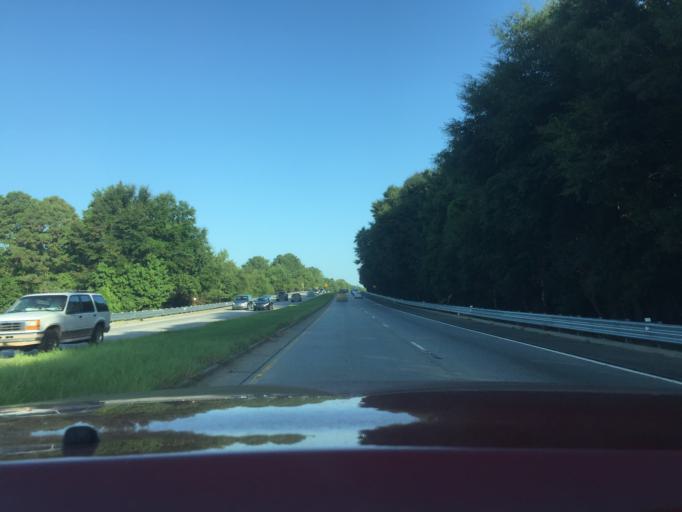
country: US
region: Georgia
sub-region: Chatham County
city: Savannah
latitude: 32.0340
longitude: -81.1304
